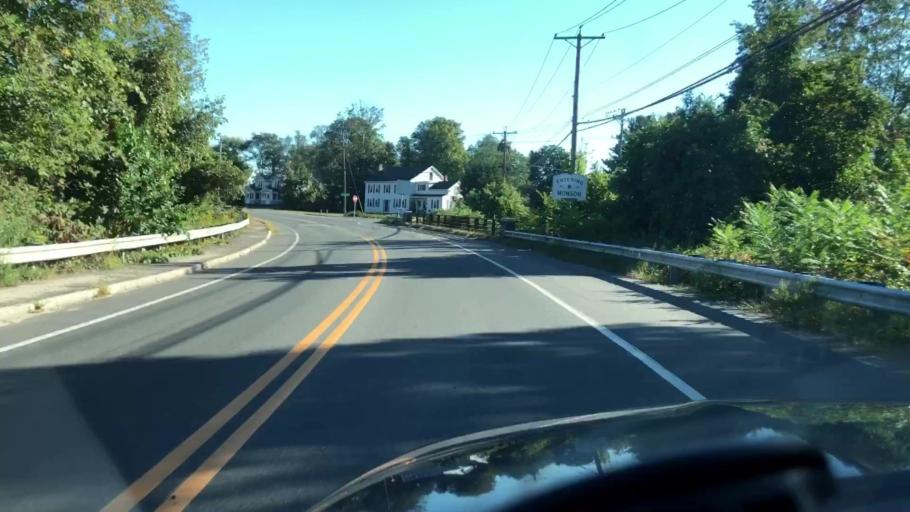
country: US
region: Massachusetts
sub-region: Hampden County
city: Palmer
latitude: 42.1445
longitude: -72.3139
